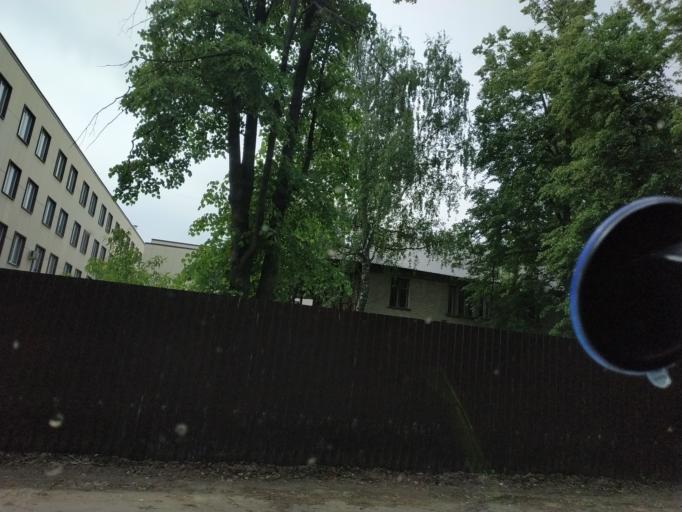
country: RU
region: Moskovskaya
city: Zhukovskiy
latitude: 55.5543
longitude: 38.1200
